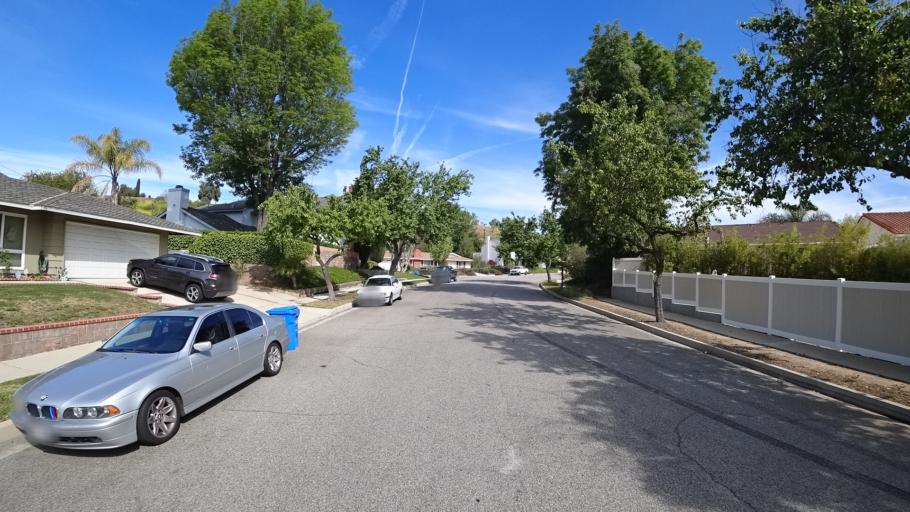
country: US
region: California
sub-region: Ventura County
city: Thousand Oaks
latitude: 34.1992
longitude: -118.8800
